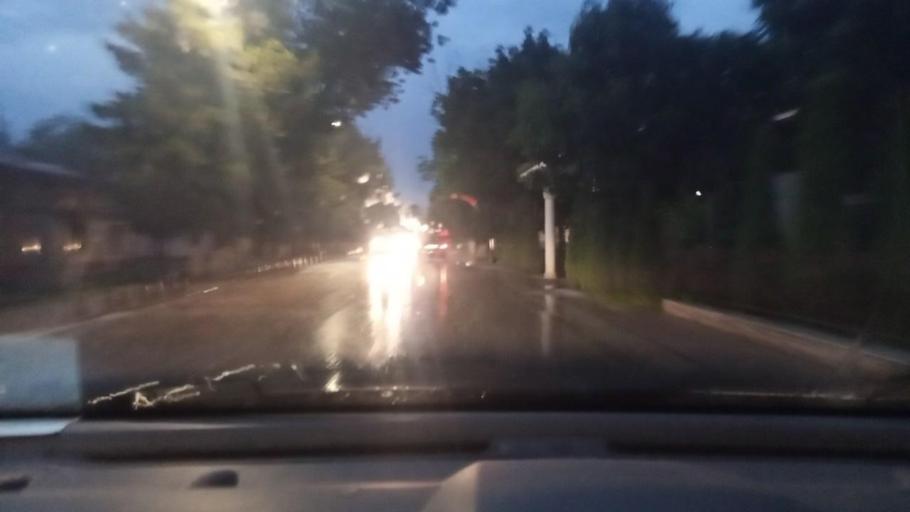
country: UZ
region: Toshkent
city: Salor
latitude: 41.3326
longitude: 69.3580
